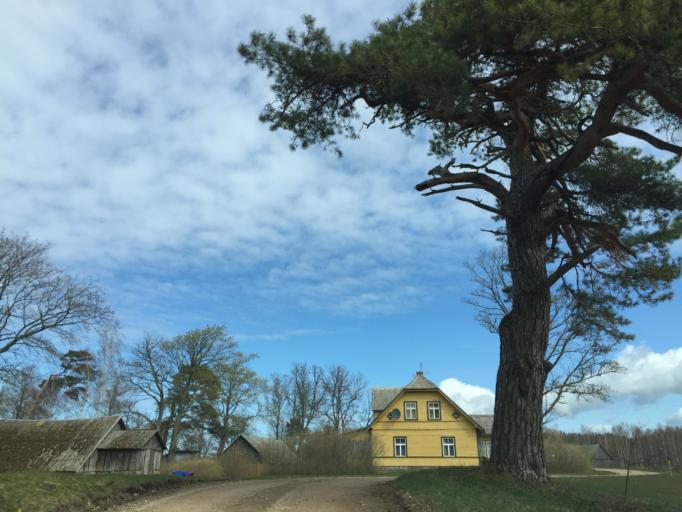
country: LV
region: Salacgrivas
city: Salacgriva
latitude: 57.5883
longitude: 24.3705
